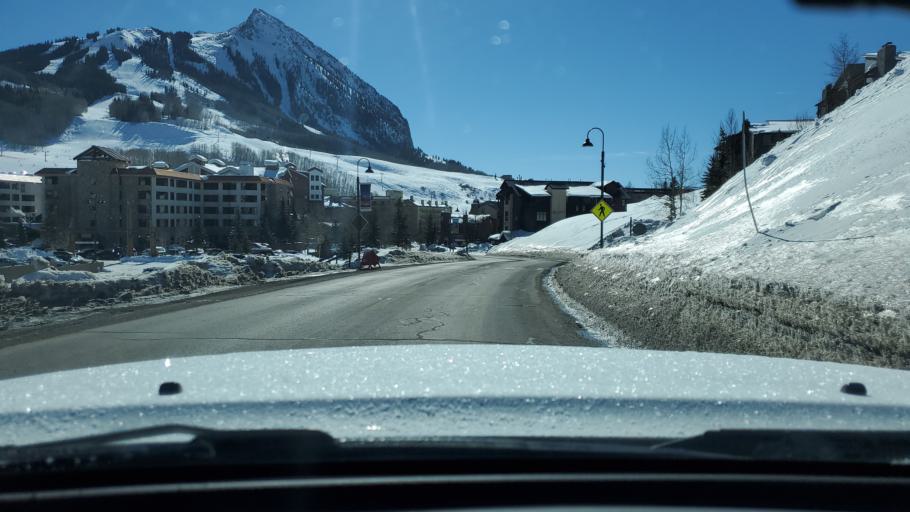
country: US
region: Colorado
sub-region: Gunnison County
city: Crested Butte
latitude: 38.9019
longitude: -106.9693
